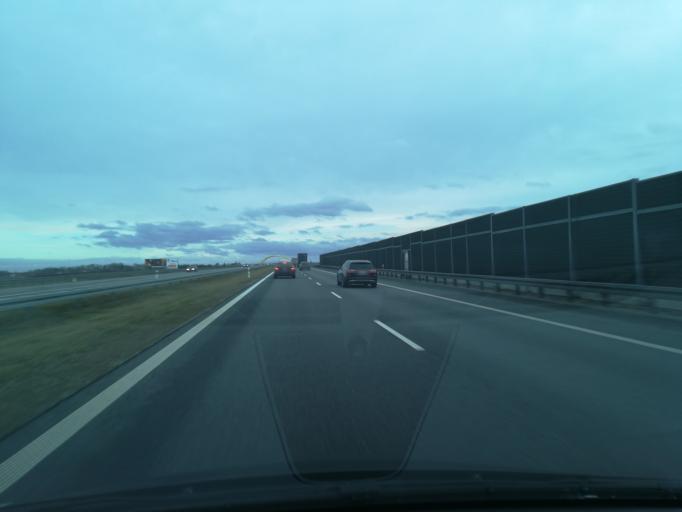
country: PL
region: Kujawsko-Pomorskie
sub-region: Powiat wloclawski
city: Chocen
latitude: 52.5781
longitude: 19.0005
